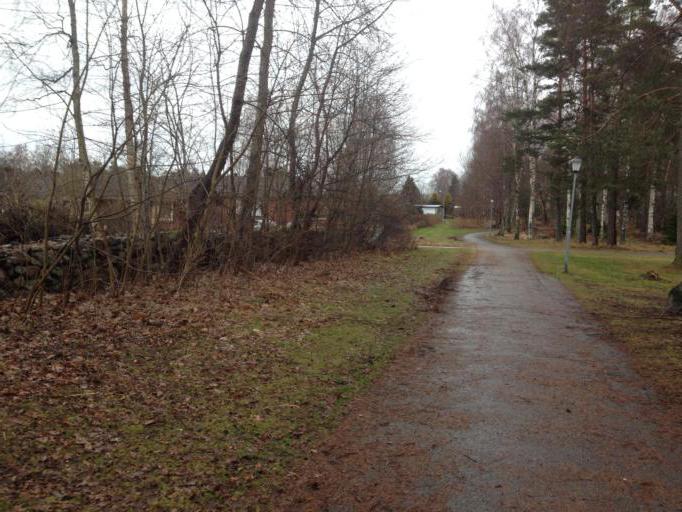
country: SE
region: Vaestra Goetaland
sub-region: Mariestads Kommun
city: Mariestad
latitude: 58.6920
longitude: 13.8043
